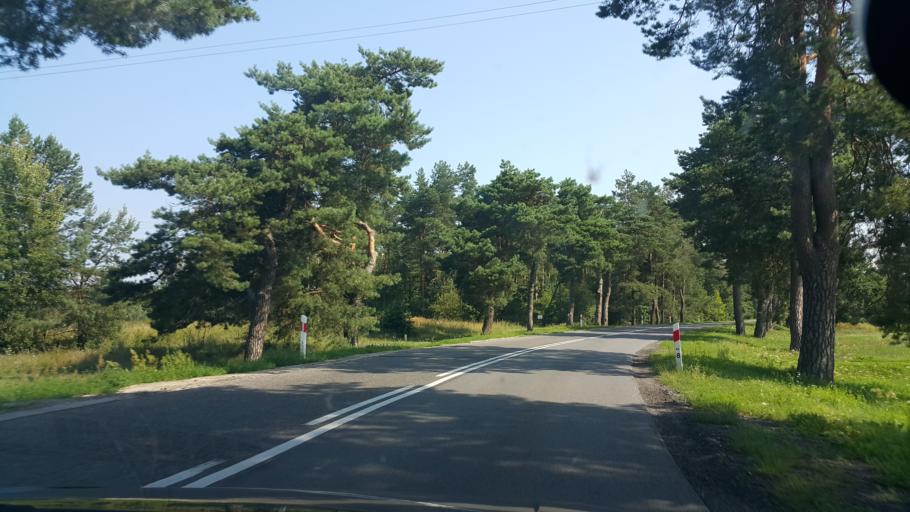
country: PL
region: Lublin Voivodeship
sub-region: Powiat wlodawski
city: Urszulin
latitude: 51.3531
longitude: 23.1598
